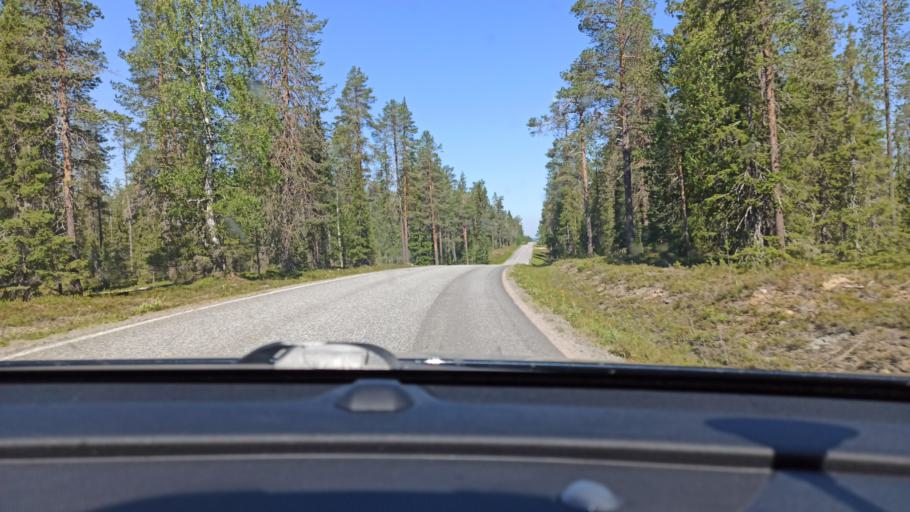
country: FI
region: Lapland
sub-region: Tunturi-Lappi
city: Kolari
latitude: 67.6710
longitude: 24.1499
